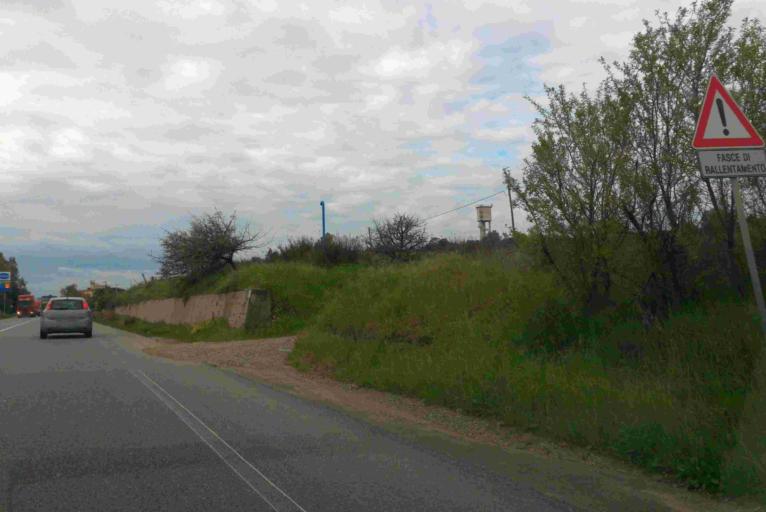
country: IT
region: Calabria
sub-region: Provincia di Catanzaro
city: Sellia Marina
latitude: 38.8903
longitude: 16.7191
